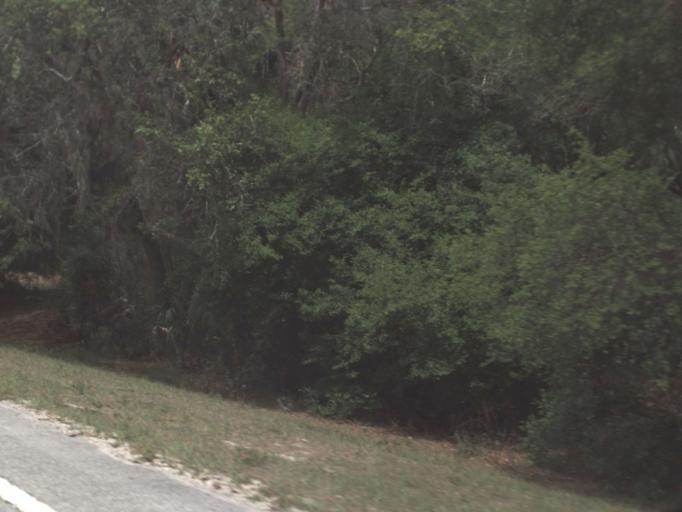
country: US
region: Florida
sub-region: Lake County
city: Mount Plymouth
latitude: 28.8876
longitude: -81.4747
